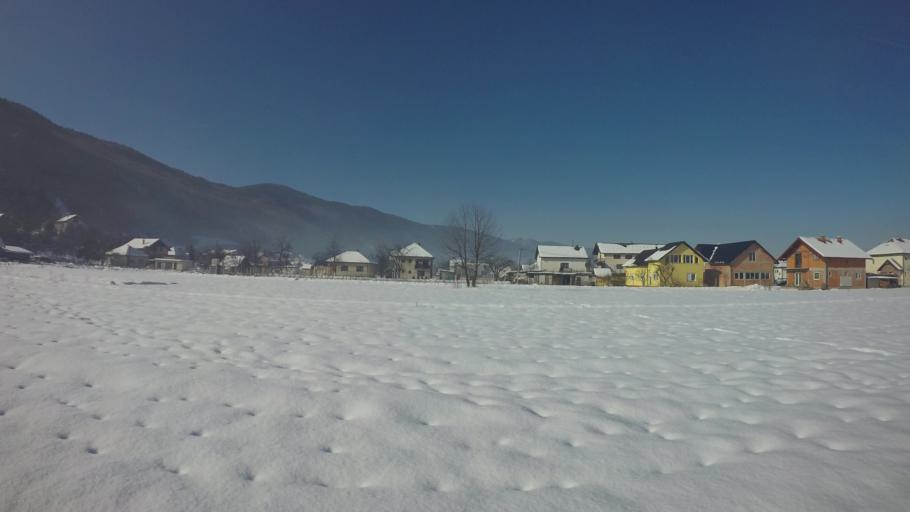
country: BA
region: Federation of Bosnia and Herzegovina
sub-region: Kanton Sarajevo
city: Sarajevo
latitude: 43.7891
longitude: 18.3411
